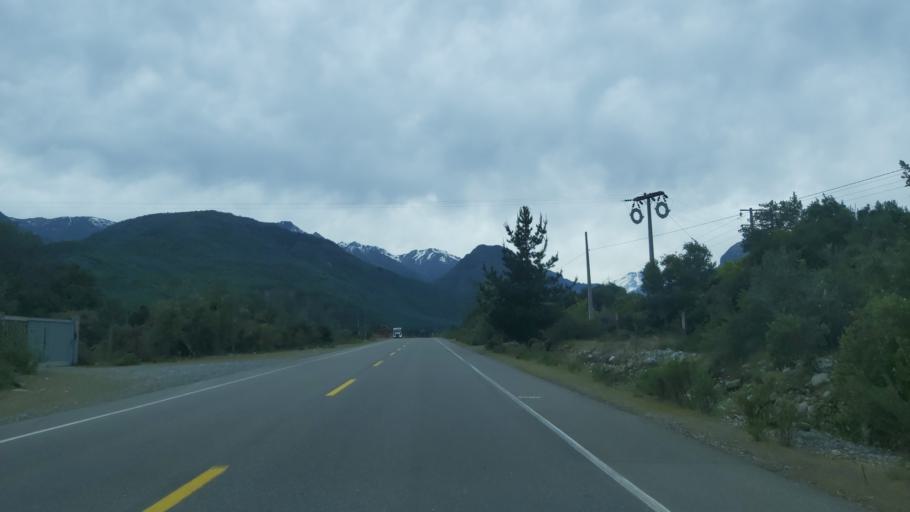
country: CL
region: Maule
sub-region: Provincia de Linares
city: Colbun
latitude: -35.7138
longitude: -71.1135
